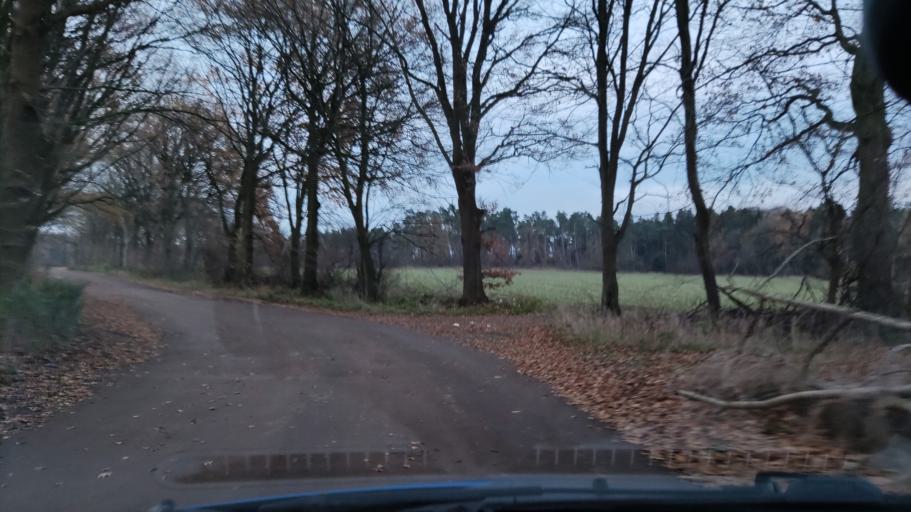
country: DE
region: Lower Saxony
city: Vogelsen
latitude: 53.2683
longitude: 10.3529
